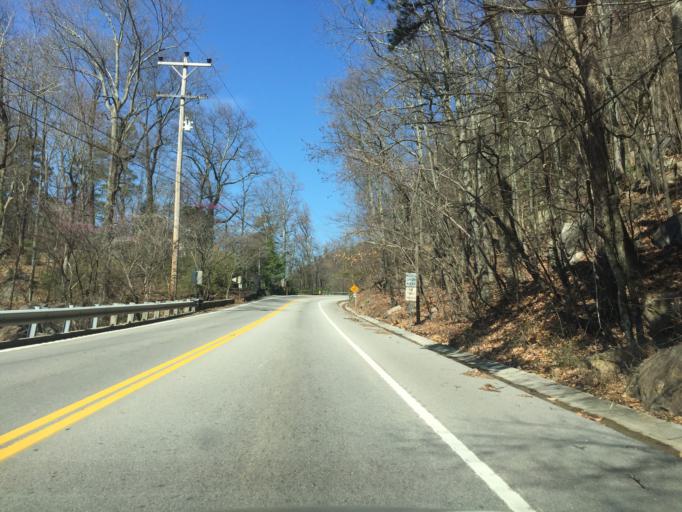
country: US
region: Tennessee
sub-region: Hamilton County
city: Signal Mountain
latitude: 35.1100
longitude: -85.3514
